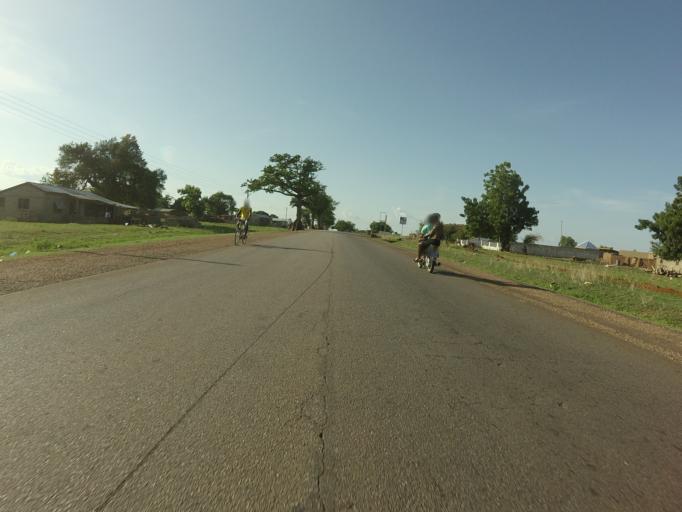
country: GH
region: Upper East
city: Navrongo
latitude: 10.9180
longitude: -1.0896
